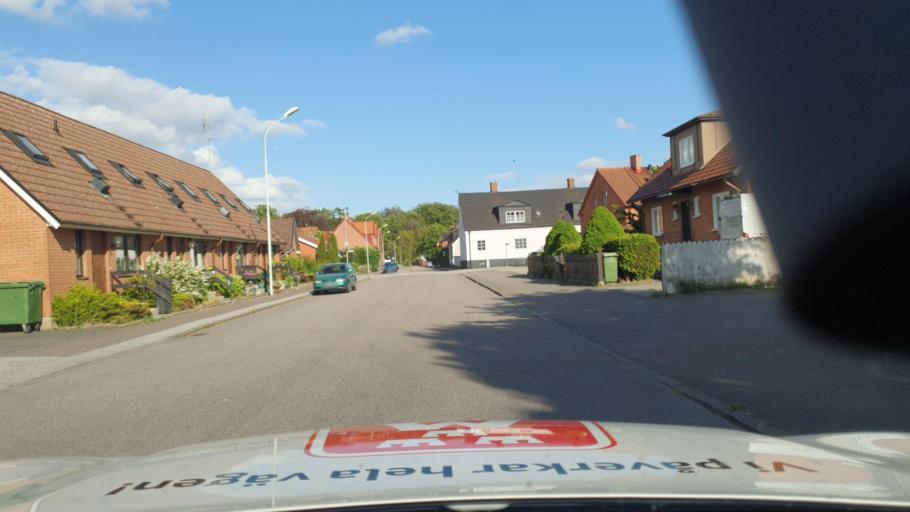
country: SE
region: Skane
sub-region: Tomelilla Kommun
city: Tomelilla
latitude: 55.5461
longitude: 13.9524
